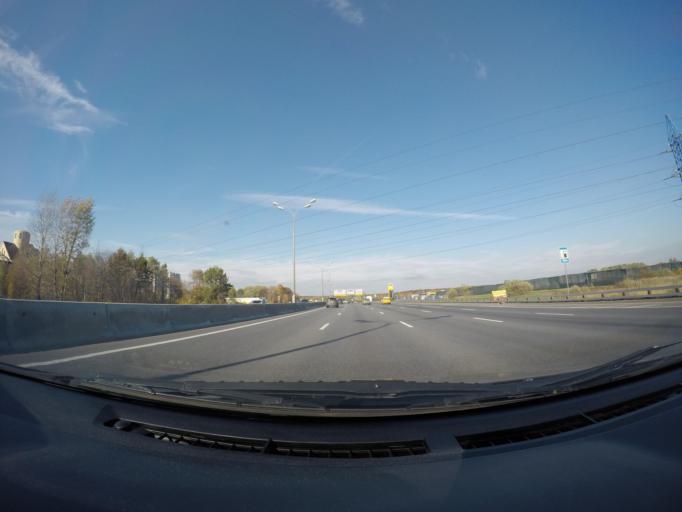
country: RU
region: Moscow
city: Gol'yanovo
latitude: 55.8240
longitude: 37.8357
